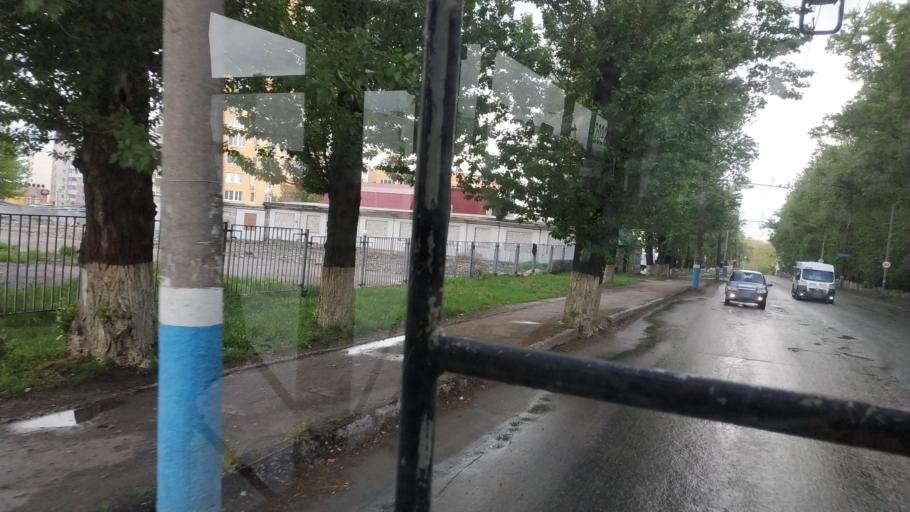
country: RU
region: Brjansk
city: Putevka
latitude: 53.2622
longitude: 34.3245
